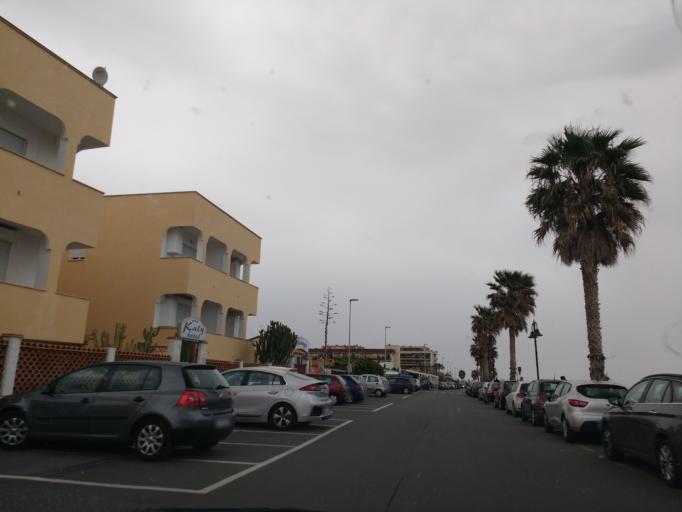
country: IT
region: Liguria
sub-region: Provincia di Imperia
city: Ventimiglia
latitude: 43.7855
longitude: 7.6215
